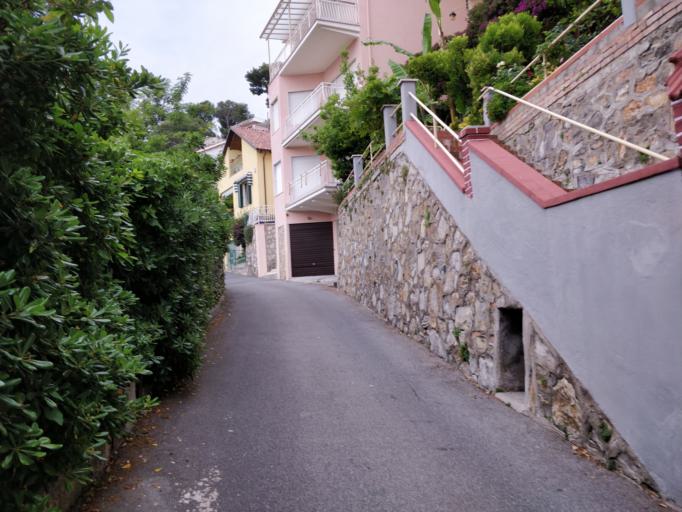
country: IT
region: Liguria
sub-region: Provincia di Savona
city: Marina di Andora
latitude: 43.9526
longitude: 8.1548
